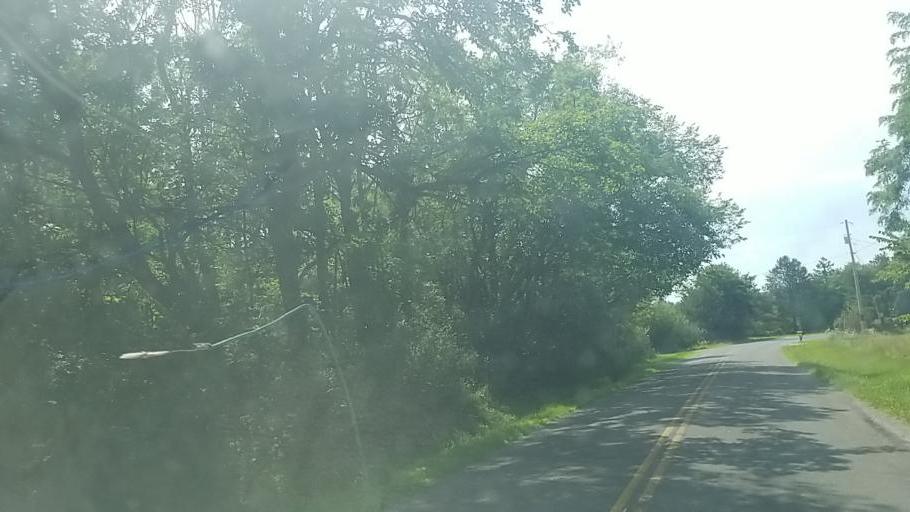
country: US
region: Ohio
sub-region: Medina County
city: Lodi
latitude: 41.0899
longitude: -81.9749
